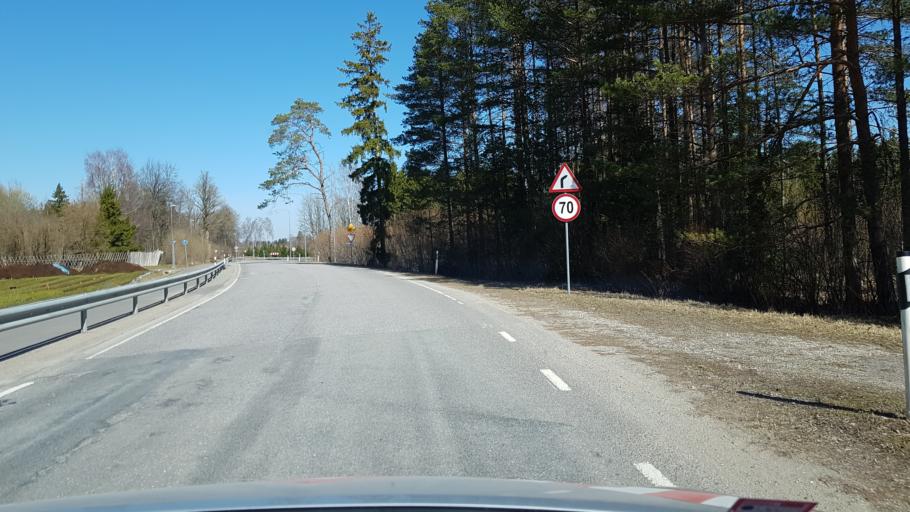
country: EE
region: Laeaene-Virumaa
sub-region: Vaeike-Maarja vald
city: Vaike-Maarja
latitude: 59.0975
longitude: 26.2248
